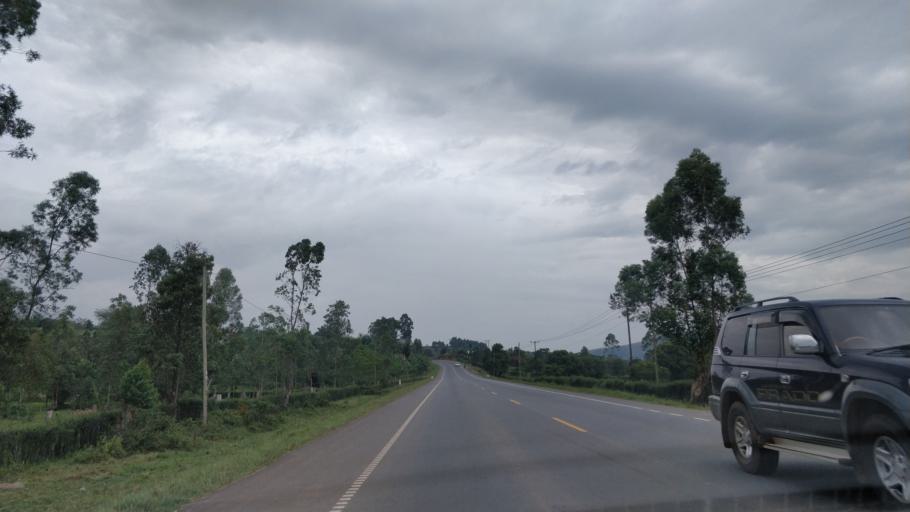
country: UG
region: Western Region
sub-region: Sheema District
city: Kibingo
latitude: -0.6562
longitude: 30.4774
